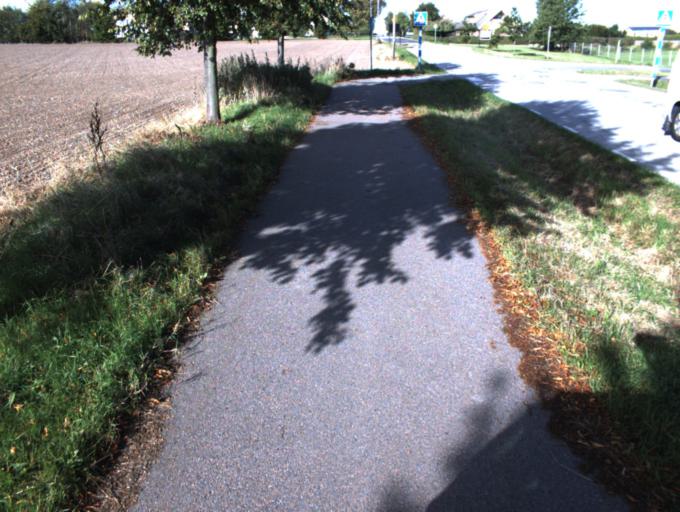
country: SE
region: Skane
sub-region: Helsingborg
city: Glumslov
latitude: 55.9619
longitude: 12.8474
